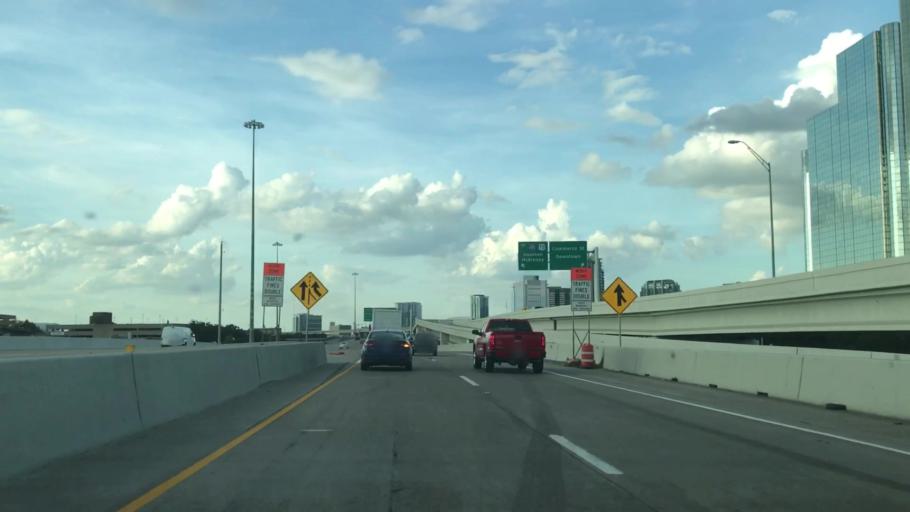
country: US
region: Texas
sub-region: Dallas County
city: Dallas
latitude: 32.7744
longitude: -96.8107
